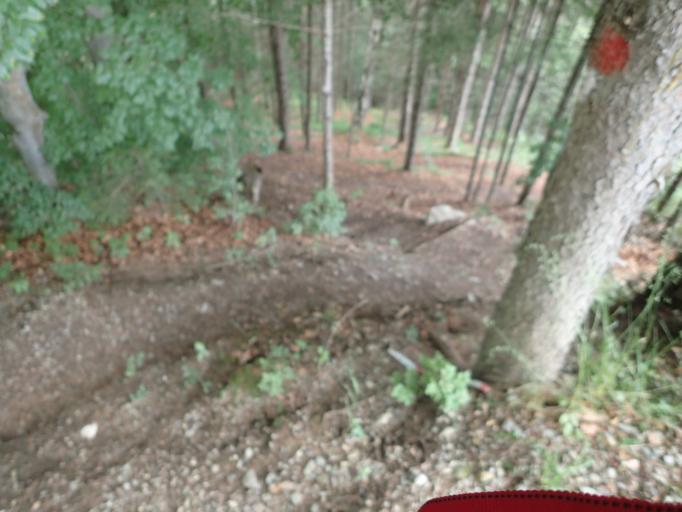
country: AT
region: Salzburg
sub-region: Politischer Bezirk Sankt Johann im Pongau
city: Muhlbach am Hochkonig
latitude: 47.3796
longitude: 13.1222
